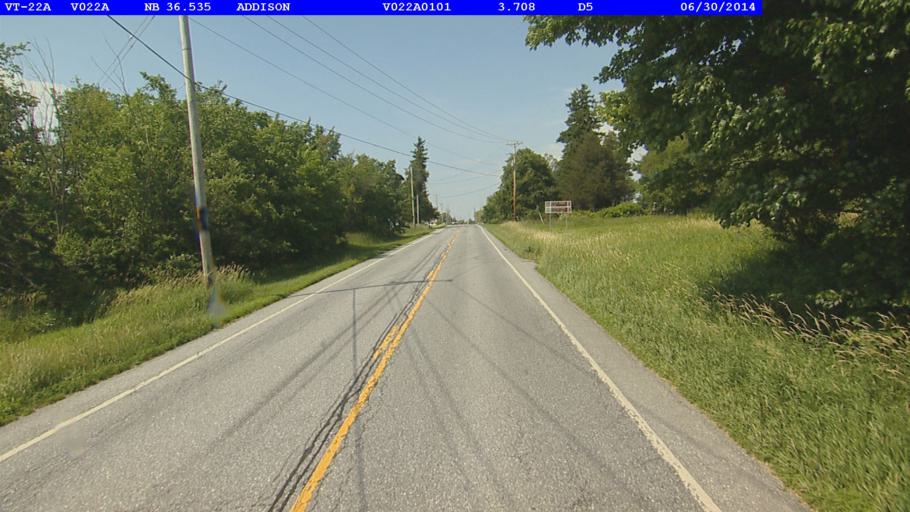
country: US
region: Vermont
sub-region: Addison County
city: Vergennes
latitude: 44.0829
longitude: -73.3029
